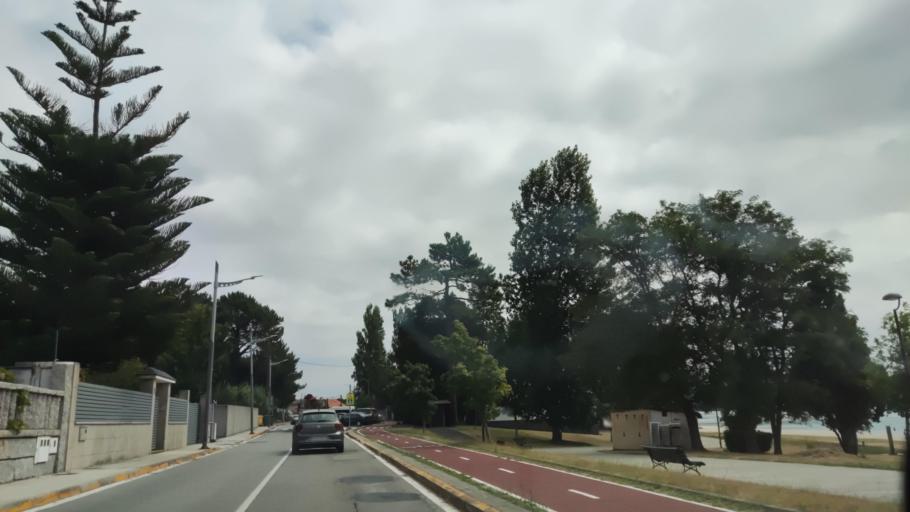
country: ES
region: Galicia
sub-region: Provincia da Coruna
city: Boiro
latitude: 42.6407
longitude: -8.8861
